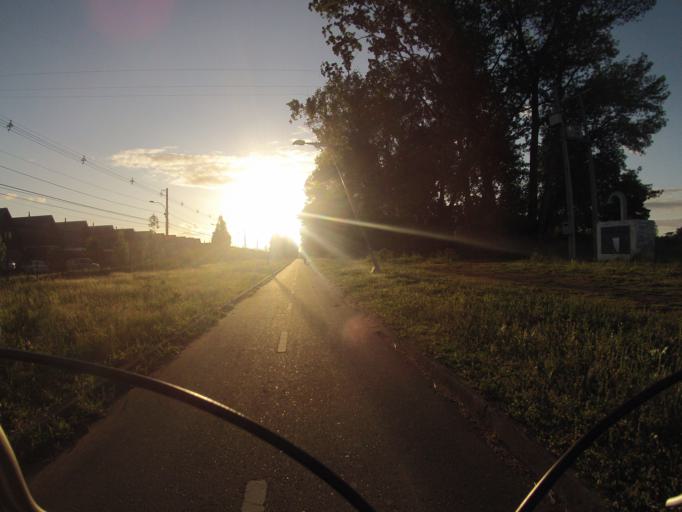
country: CL
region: Araucania
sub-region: Provincia de Cautin
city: Temuco
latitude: -38.7529
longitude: -72.6535
